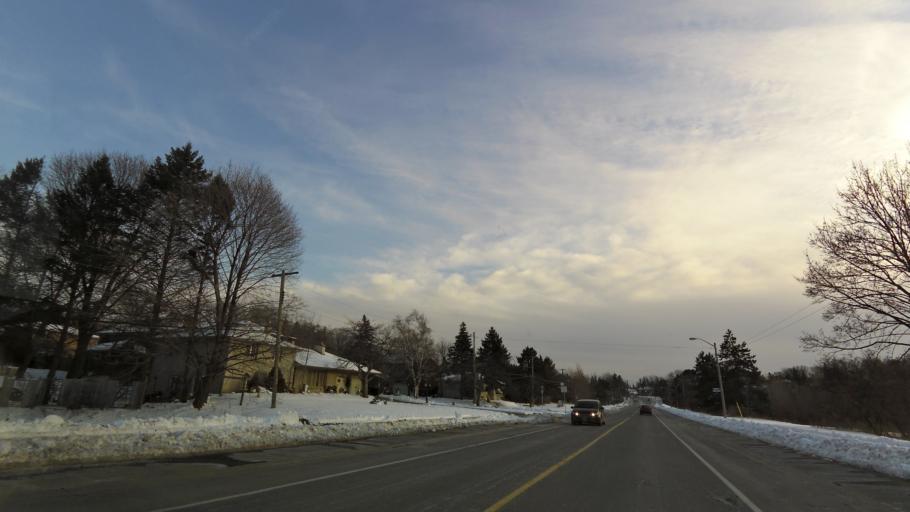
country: CA
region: Ontario
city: Etobicoke
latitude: 43.6607
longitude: -79.5569
